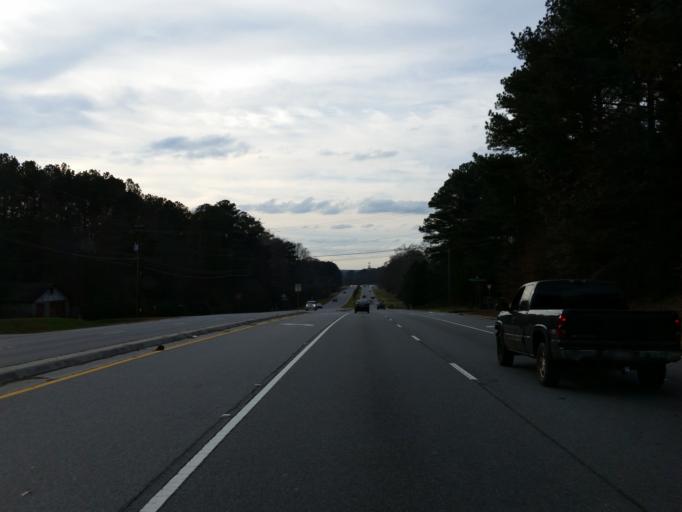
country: US
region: Georgia
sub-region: Cobb County
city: Fair Oaks
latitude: 33.9045
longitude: -84.6102
